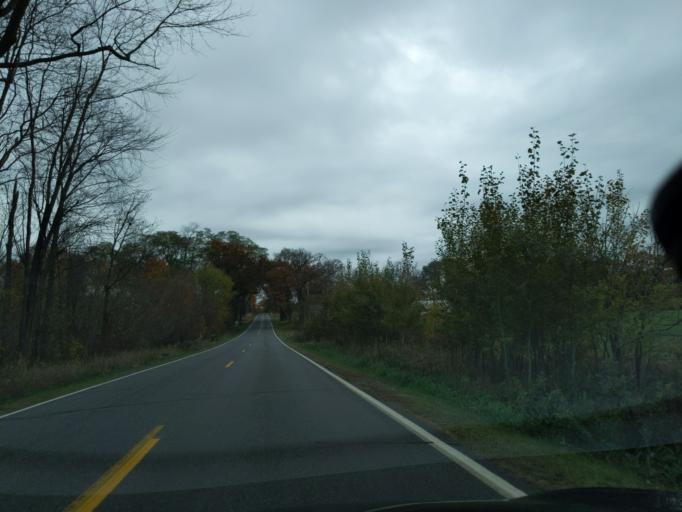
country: US
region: Michigan
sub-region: Eaton County
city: Eaton Rapids
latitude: 42.3632
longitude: -84.6005
